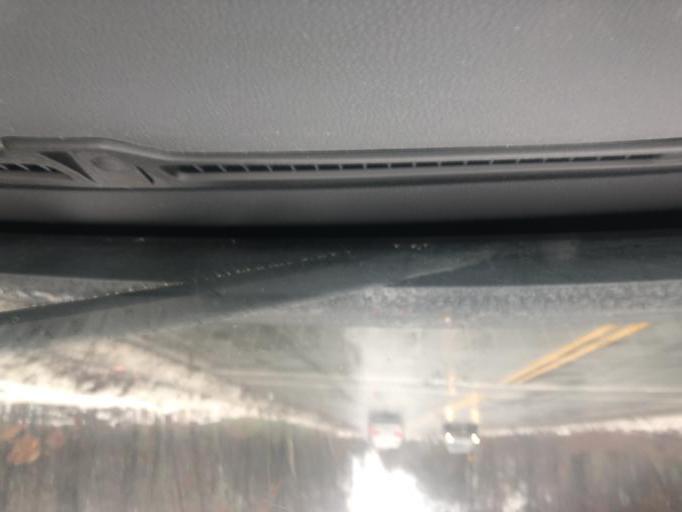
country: US
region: Massachusetts
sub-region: Norfolk County
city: Avon
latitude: 42.1017
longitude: -71.0465
